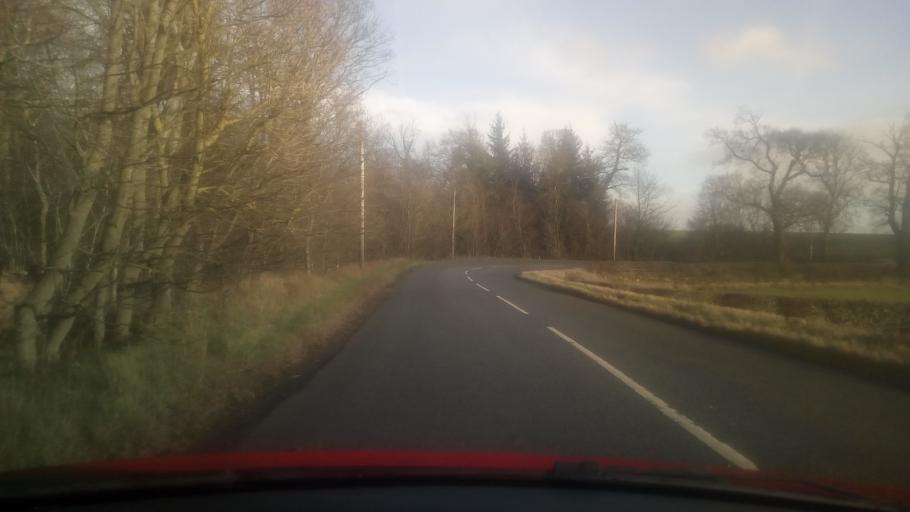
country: GB
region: Scotland
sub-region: The Scottish Borders
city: Kelso
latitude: 55.6626
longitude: -2.3833
